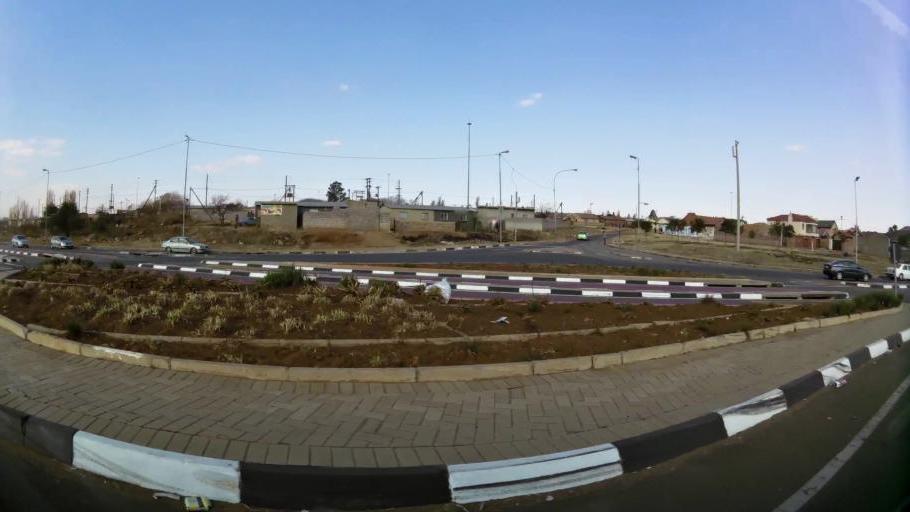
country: ZA
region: Gauteng
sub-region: City of Johannesburg Metropolitan Municipality
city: Soweto
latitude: -26.2550
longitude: 27.8937
